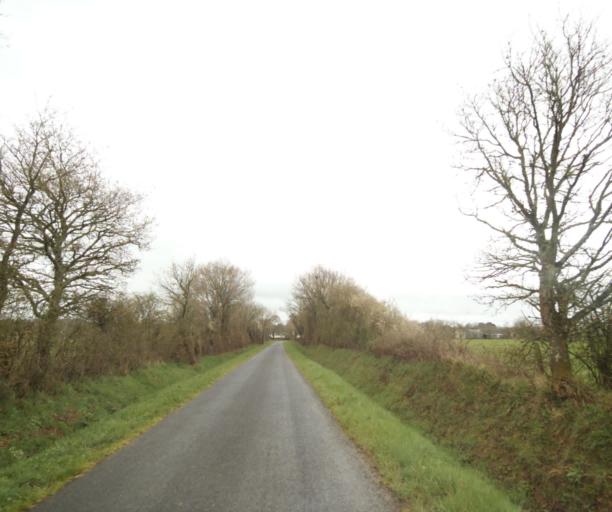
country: FR
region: Pays de la Loire
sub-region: Departement de la Loire-Atlantique
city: Bouvron
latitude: 47.4433
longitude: -1.8455
